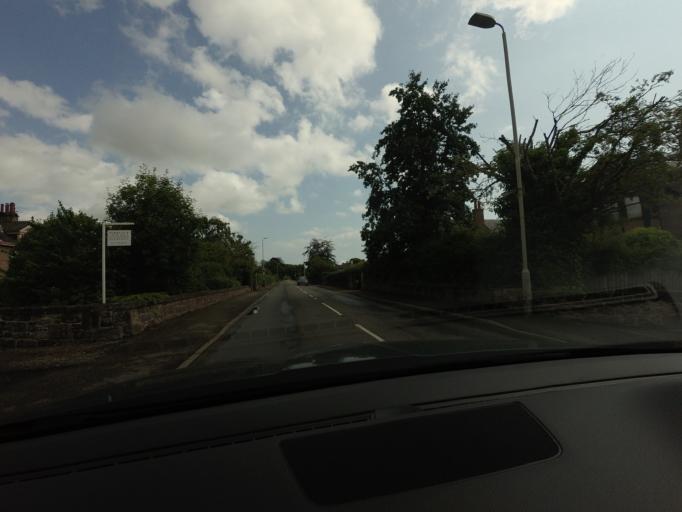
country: GB
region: Scotland
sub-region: Highland
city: Dingwall
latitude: 57.6012
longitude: -4.4278
